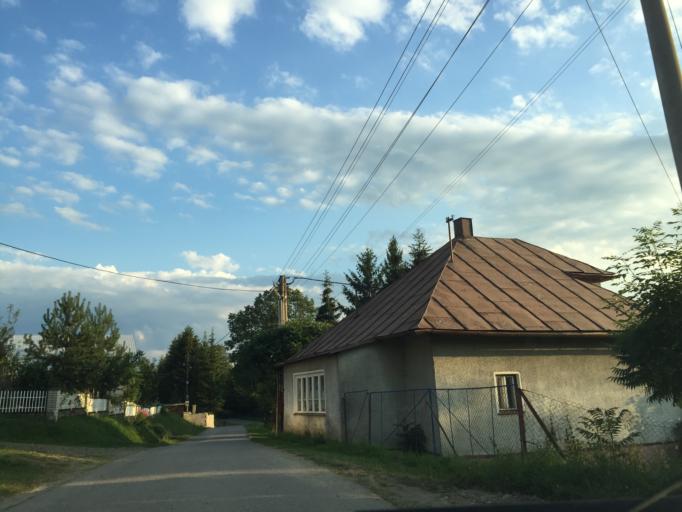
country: PL
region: Silesian Voivodeship
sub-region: Powiat zywiecki
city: Korbielow
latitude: 49.4796
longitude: 19.3830
